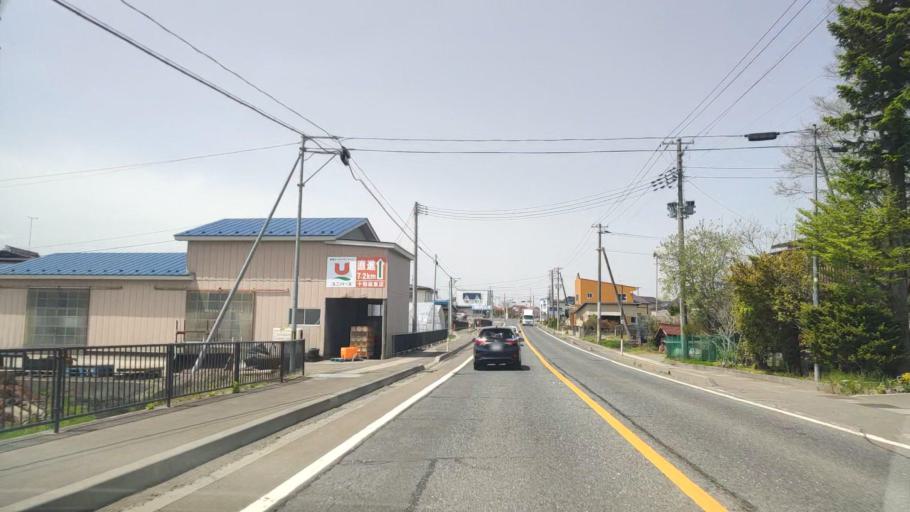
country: JP
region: Aomori
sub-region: Misawa Shi
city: Inuotose
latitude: 40.6067
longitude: 141.2890
